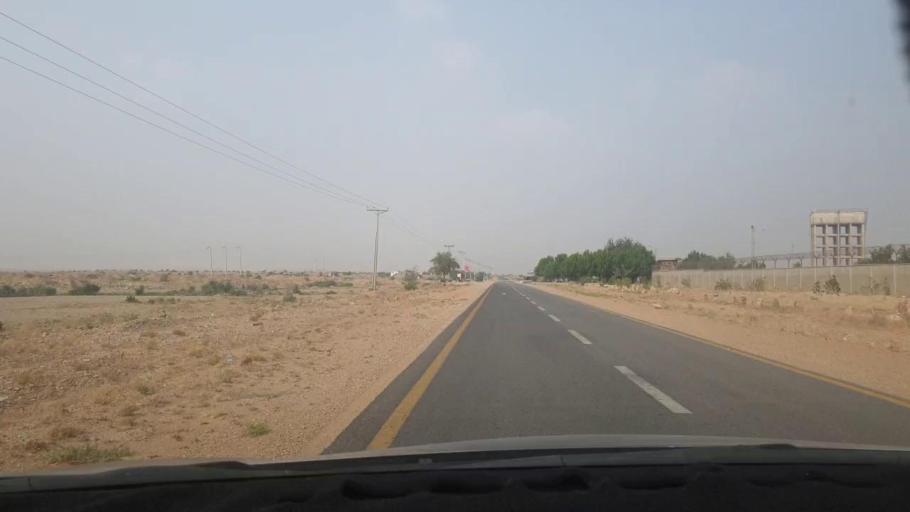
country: PK
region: Sindh
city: Jamshoro
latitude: 25.5591
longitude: 68.3189
